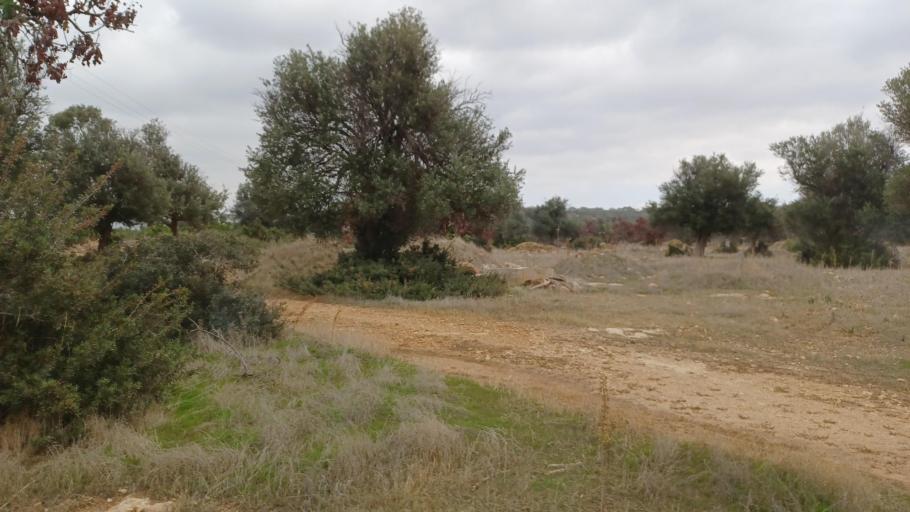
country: CY
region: Pafos
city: Pegeia
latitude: 34.9040
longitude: 32.3350
